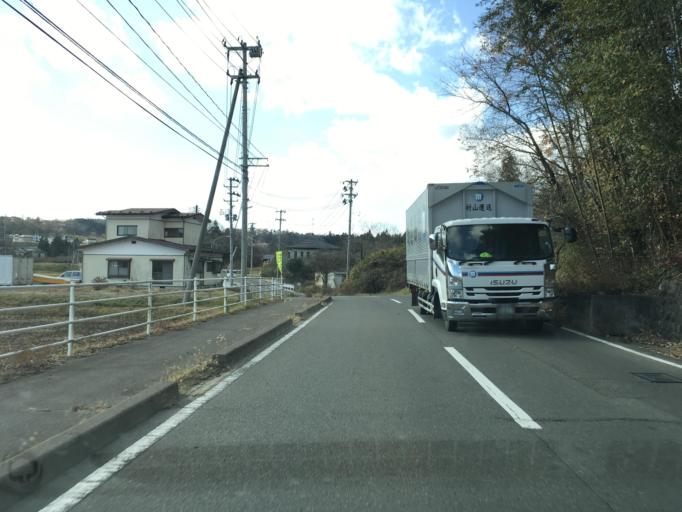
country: JP
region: Miyagi
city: Sendai
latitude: 38.2955
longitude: 140.7660
